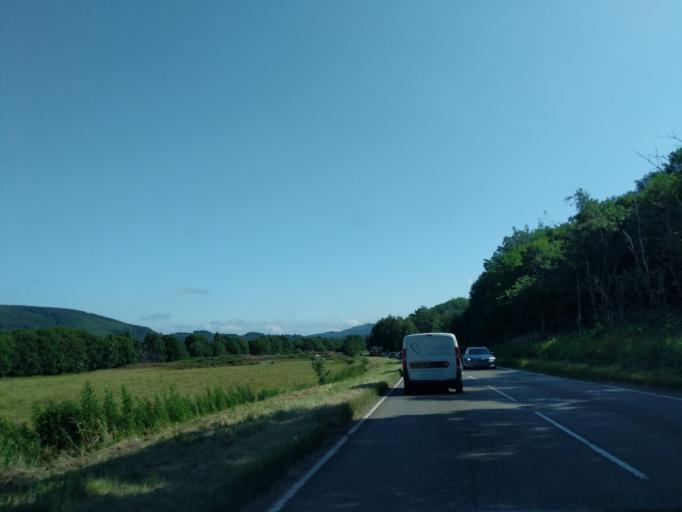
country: GB
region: Scotland
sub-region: Moray
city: Rothes
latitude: 57.5164
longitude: -3.2084
